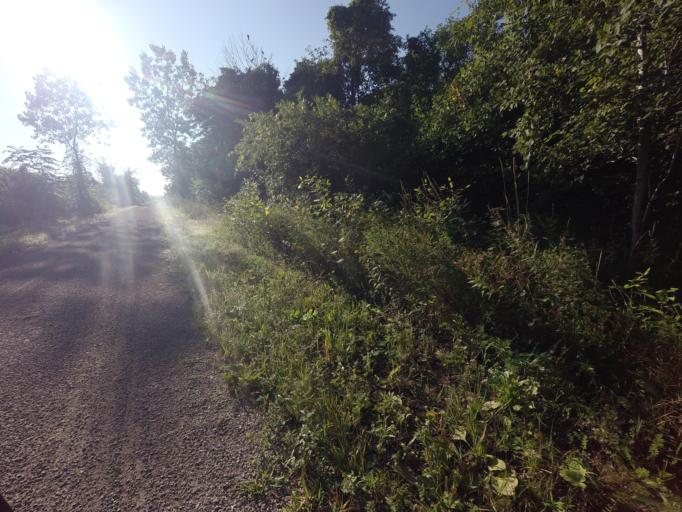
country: CA
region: Ontario
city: Goderich
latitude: 43.7639
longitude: -81.5298
